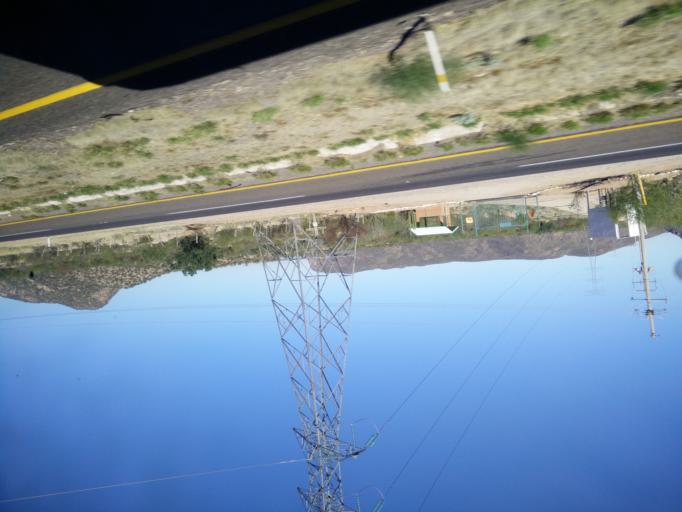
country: MX
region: Sonora
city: Hermosillo
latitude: 28.9689
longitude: -110.9636
